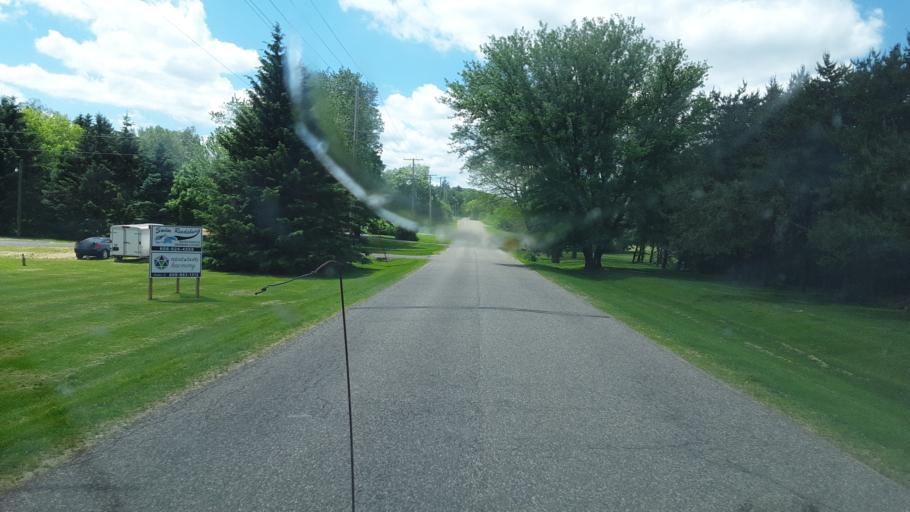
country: US
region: Wisconsin
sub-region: Sauk County
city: Reedsburg
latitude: 43.5623
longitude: -89.9746
